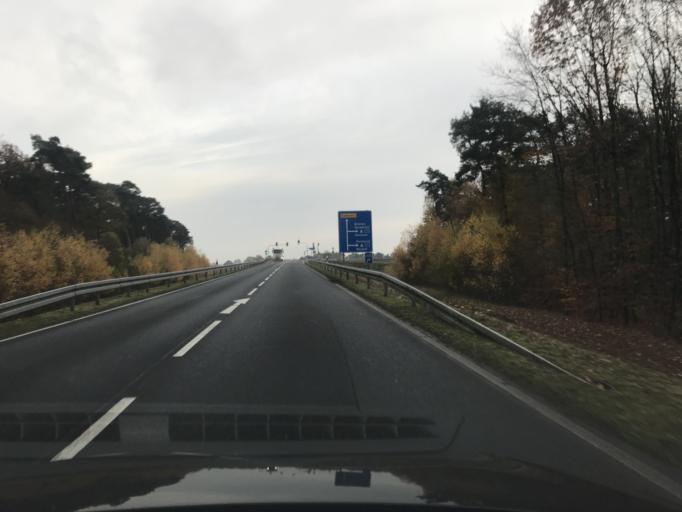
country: DE
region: North Rhine-Westphalia
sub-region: Regierungsbezirk Munster
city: Ladbergen
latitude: 52.1163
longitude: 7.6988
